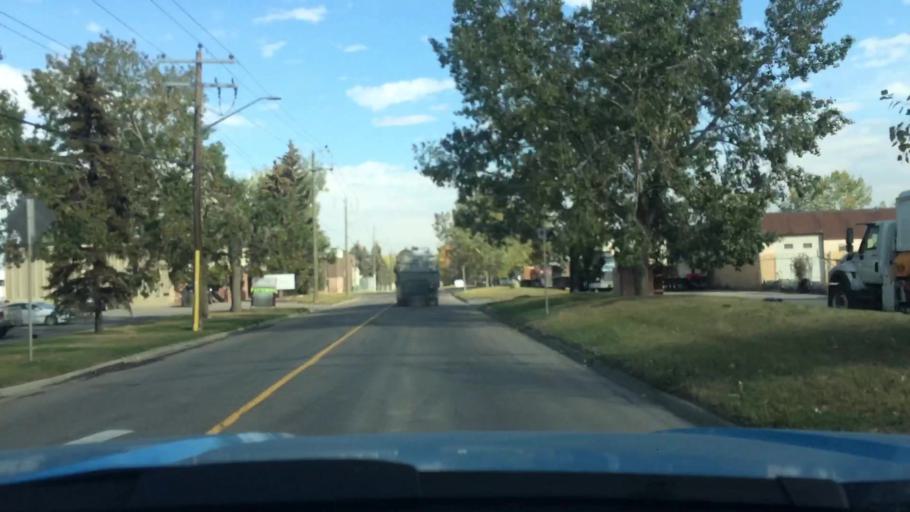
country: CA
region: Alberta
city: Calgary
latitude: 50.9955
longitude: -113.9765
